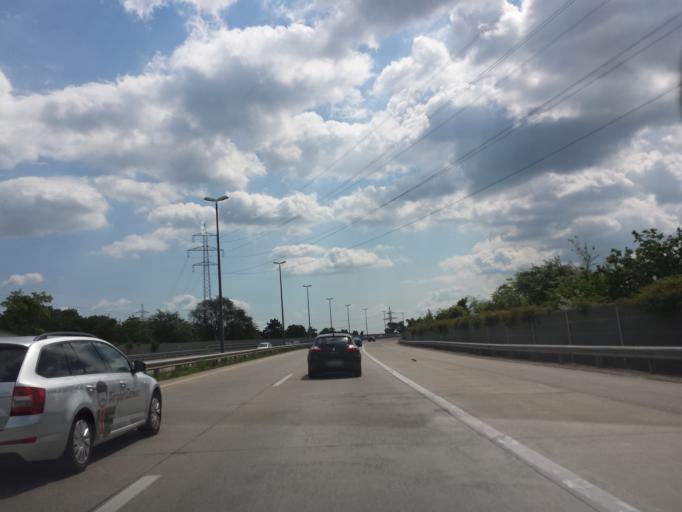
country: AT
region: Lower Austria
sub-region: Politischer Bezirk Wien-Umgebung
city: Schwechat
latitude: 48.1650
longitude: 16.4708
